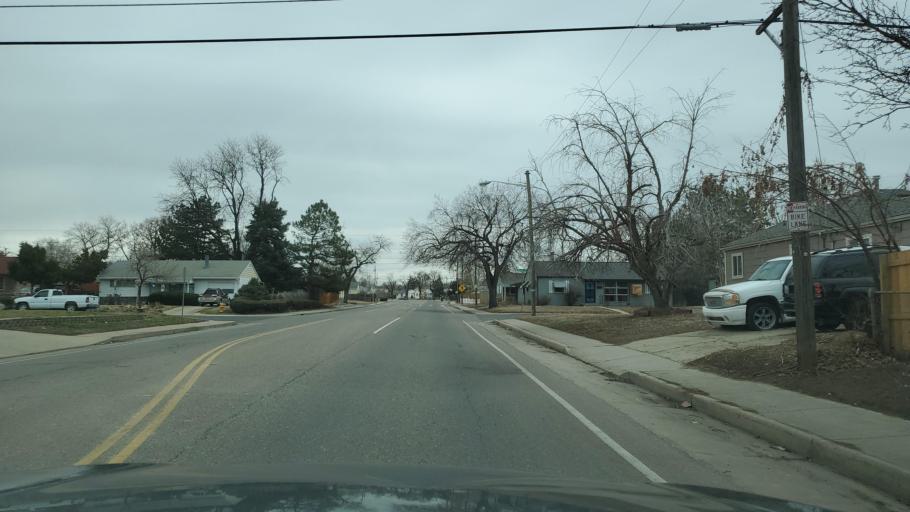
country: US
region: Colorado
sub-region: Adams County
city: Aurora
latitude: 39.7289
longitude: -104.8573
